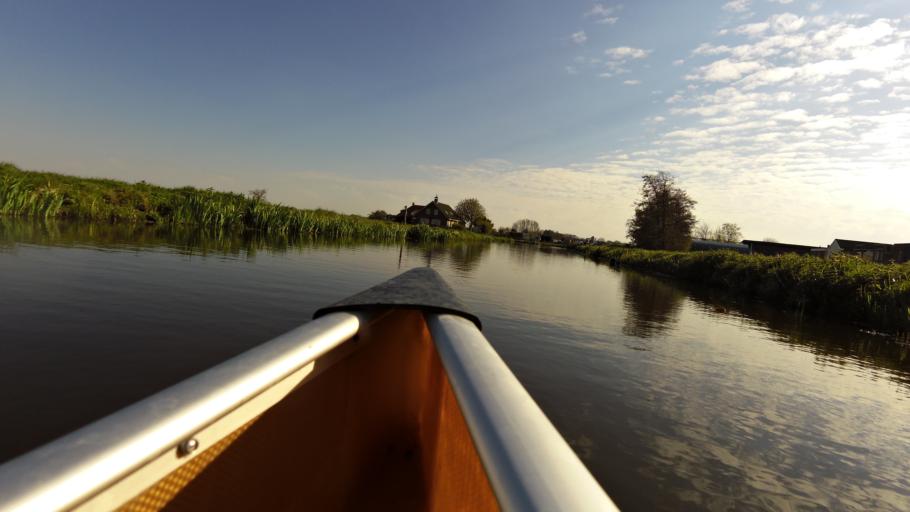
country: NL
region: South Holland
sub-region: Gemeente Teylingen
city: Sassenheim
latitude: 52.2372
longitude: 4.5401
